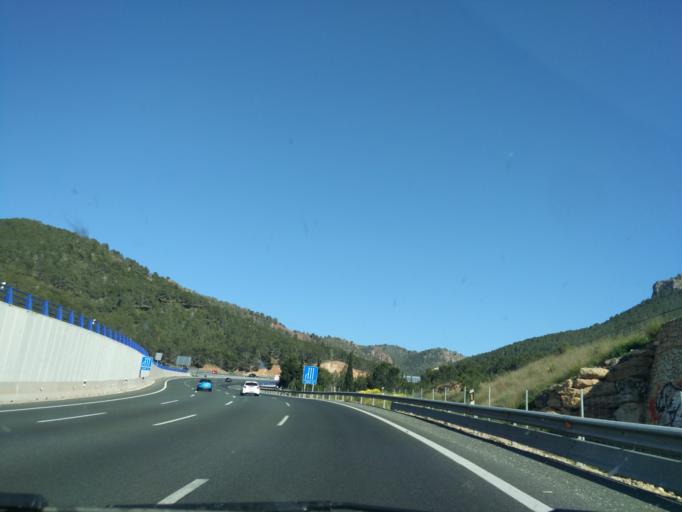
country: ES
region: Murcia
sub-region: Murcia
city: Alcantarilla
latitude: 37.9088
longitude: -1.1615
